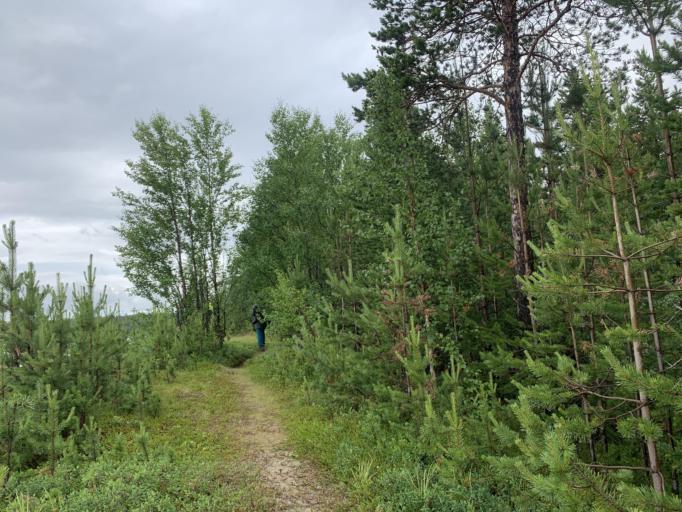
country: RU
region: Murmansk
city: Monchegorsk
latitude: 67.9501
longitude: 33.0217
